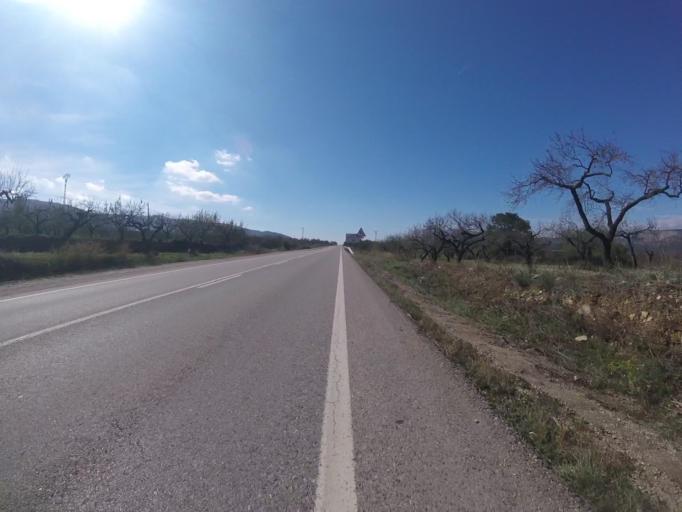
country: ES
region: Valencia
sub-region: Provincia de Castello
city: Albocasser
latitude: 40.3418
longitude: -0.0072
